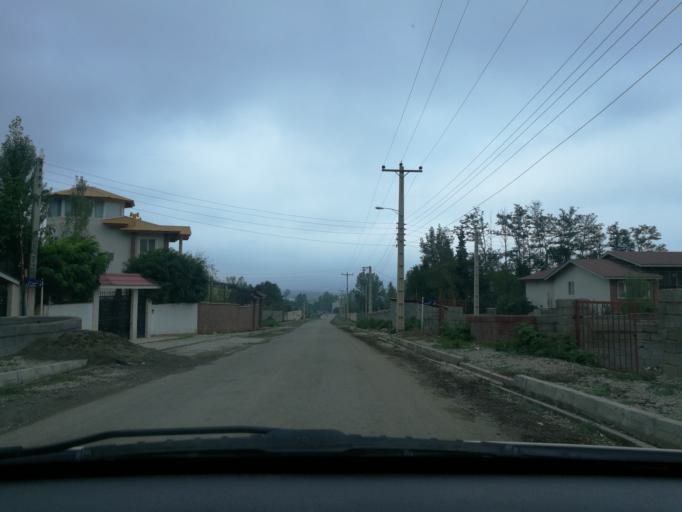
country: IR
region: Mazandaran
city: `Abbasabad
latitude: 36.4979
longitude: 51.2165
